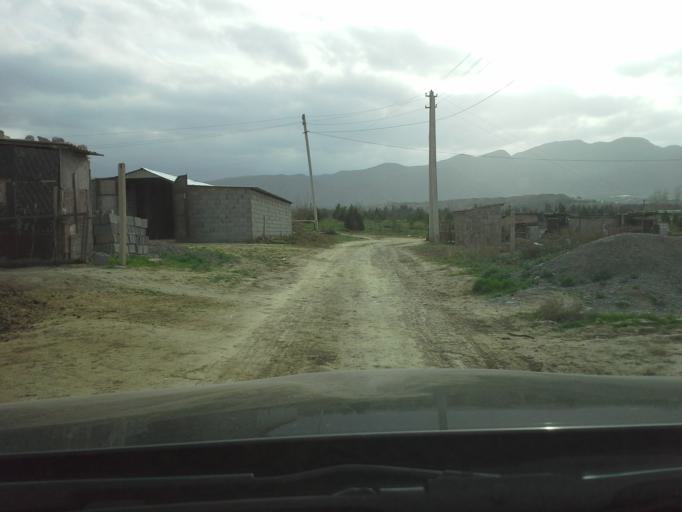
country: TM
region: Ahal
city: Abadan
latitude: 37.9591
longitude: 58.2301
